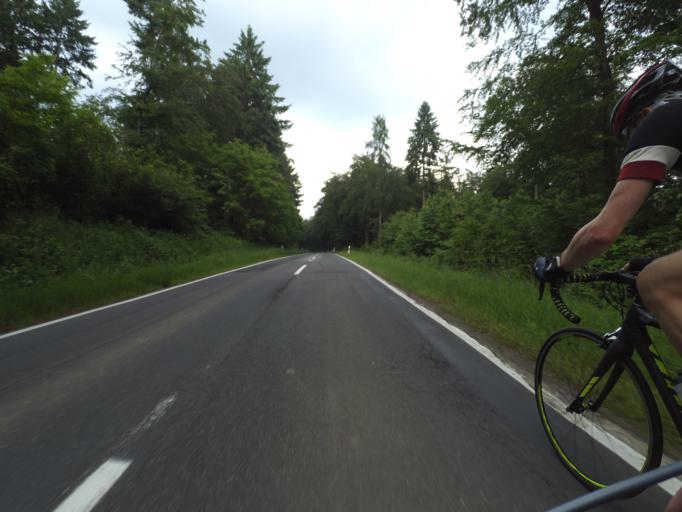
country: DE
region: Rheinland-Pfalz
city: Lutz
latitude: 50.1625
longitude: 7.3340
